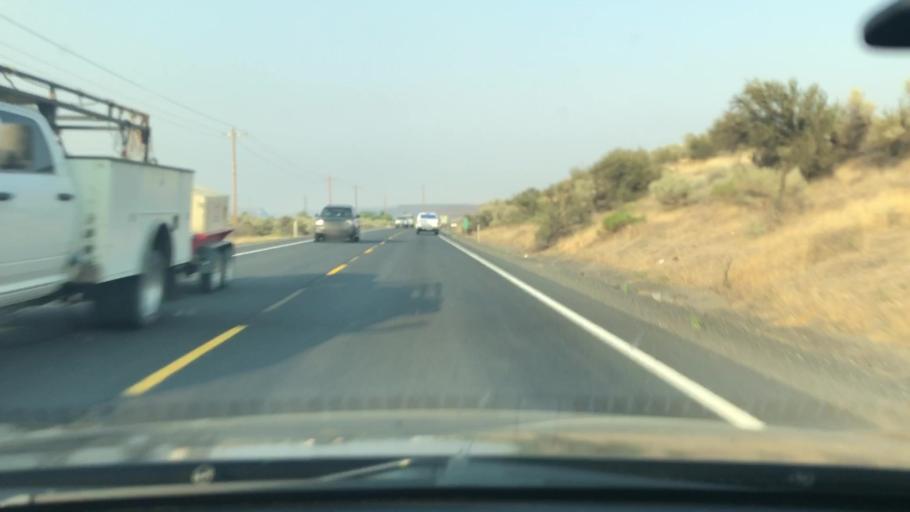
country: US
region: Oregon
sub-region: Umatilla County
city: Stanfield
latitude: 45.9192
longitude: -119.1257
